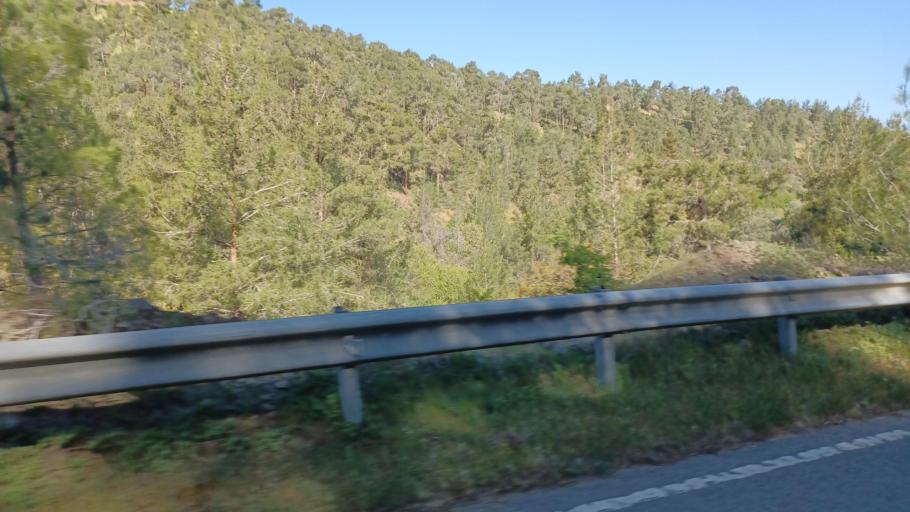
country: CY
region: Limassol
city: Kyperounta
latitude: 35.0206
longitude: 33.0376
